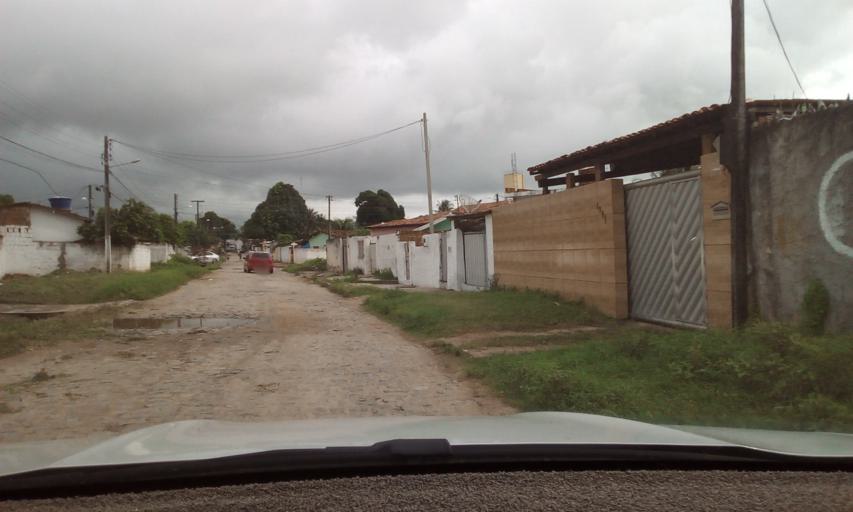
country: BR
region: Paraiba
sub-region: Bayeux
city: Bayeux
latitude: -7.1516
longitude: -34.9027
